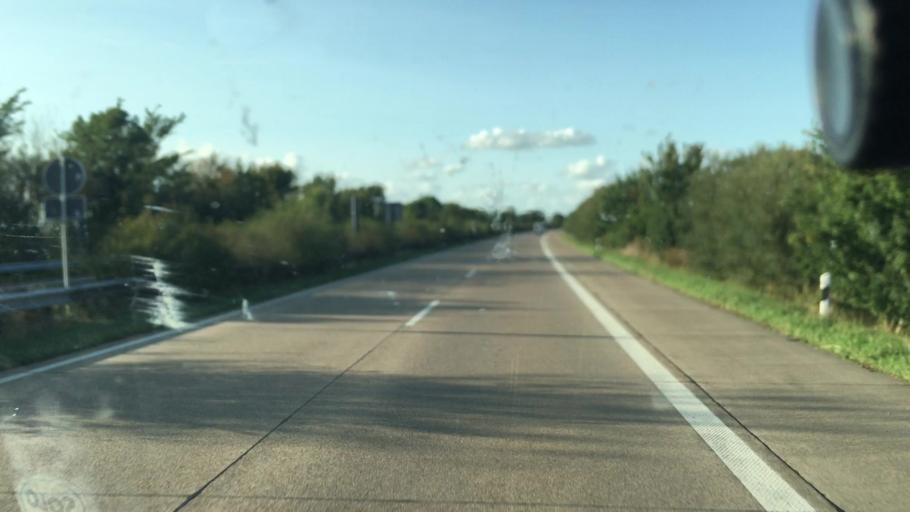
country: DE
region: Lower Saxony
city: Sande
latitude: 53.4539
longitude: 8.0210
